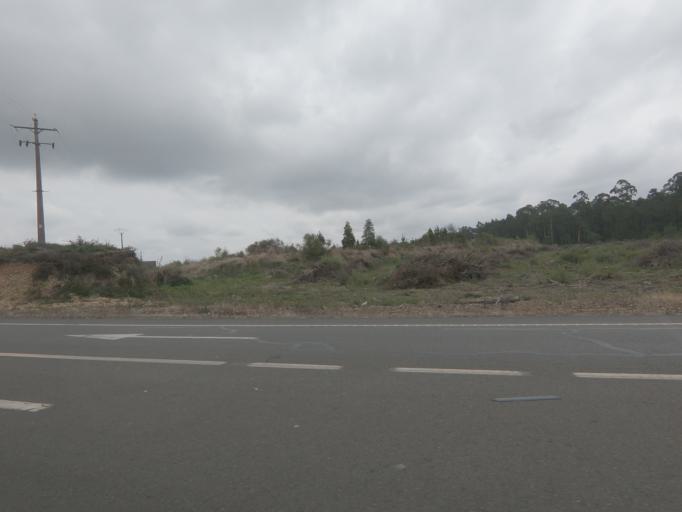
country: ES
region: Galicia
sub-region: Provincia de Pontevedra
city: Tomino
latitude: 41.9877
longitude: -8.7164
